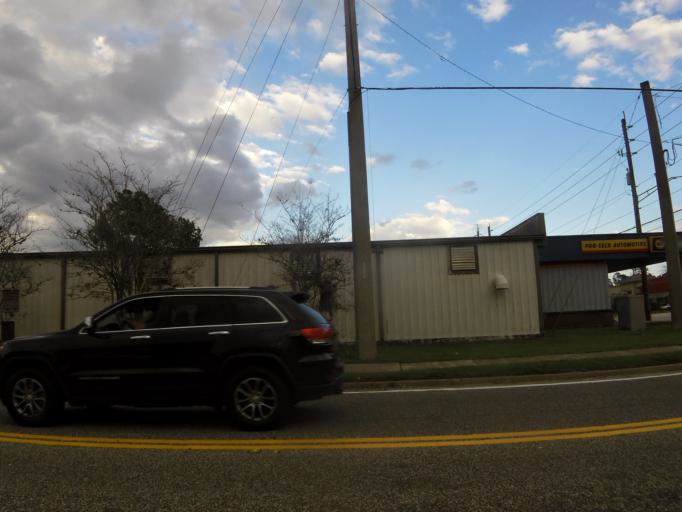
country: US
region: Florida
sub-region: Saint Johns County
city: Fruit Cove
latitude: 30.2062
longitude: -81.5834
